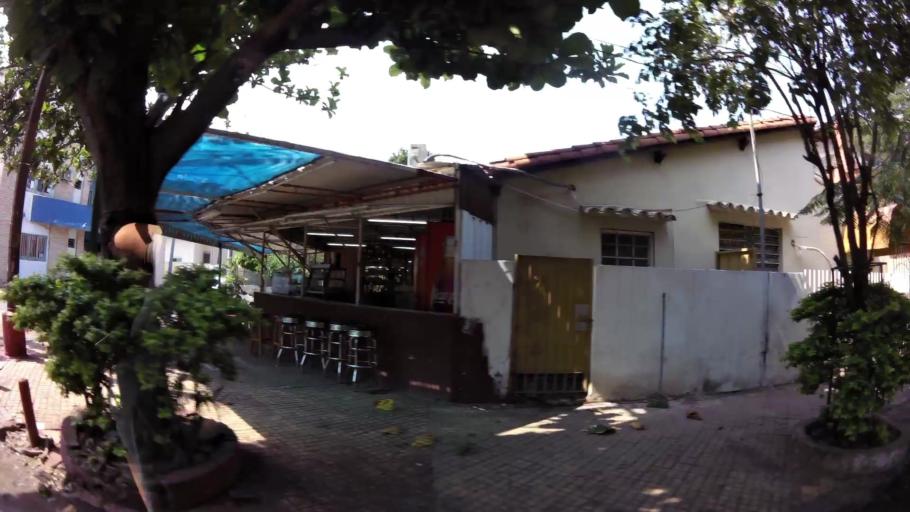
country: PY
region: Presidente Hayes
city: Nanawa
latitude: -25.2880
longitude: -57.6564
